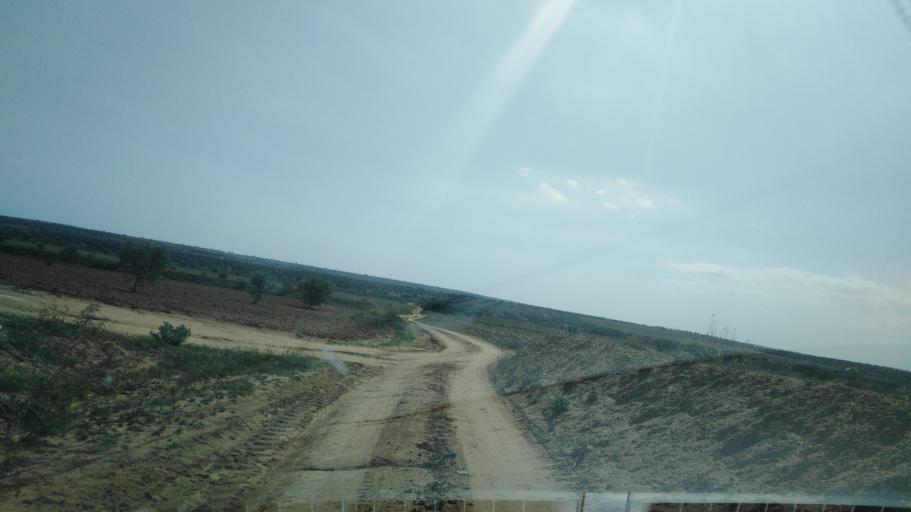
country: TN
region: Safaqis
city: Bi'r `Ali Bin Khalifah
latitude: 34.7834
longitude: 10.3679
